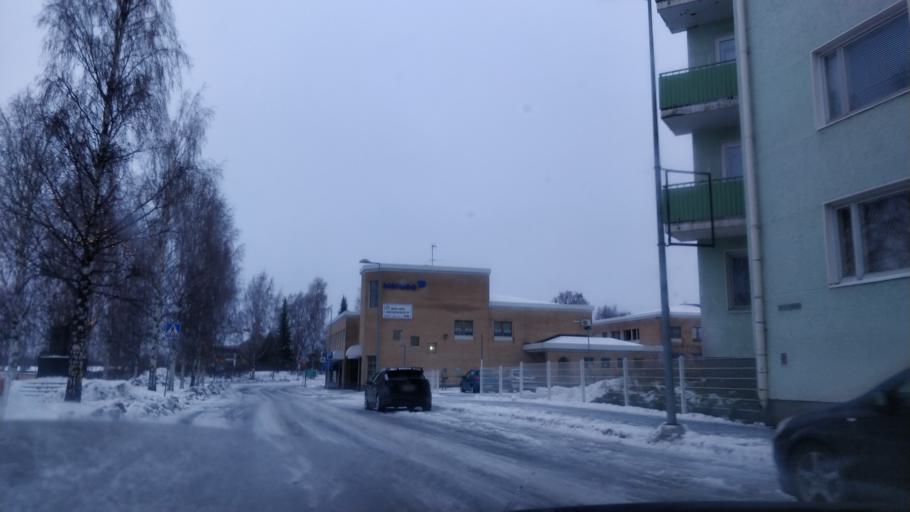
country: FI
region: Lapland
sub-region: Kemi-Tornio
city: Kemi
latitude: 65.7379
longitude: 24.5611
